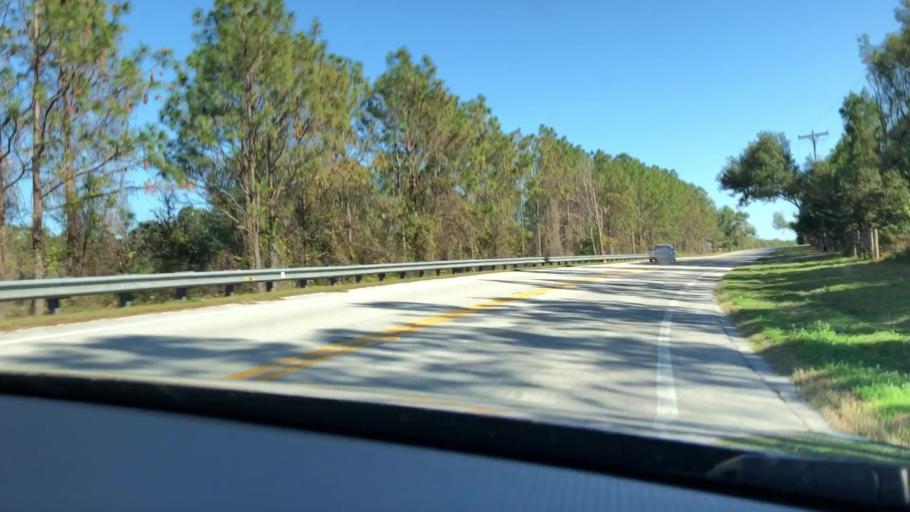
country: US
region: Florida
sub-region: Lake County
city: Eustis
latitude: 28.8719
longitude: -81.6322
